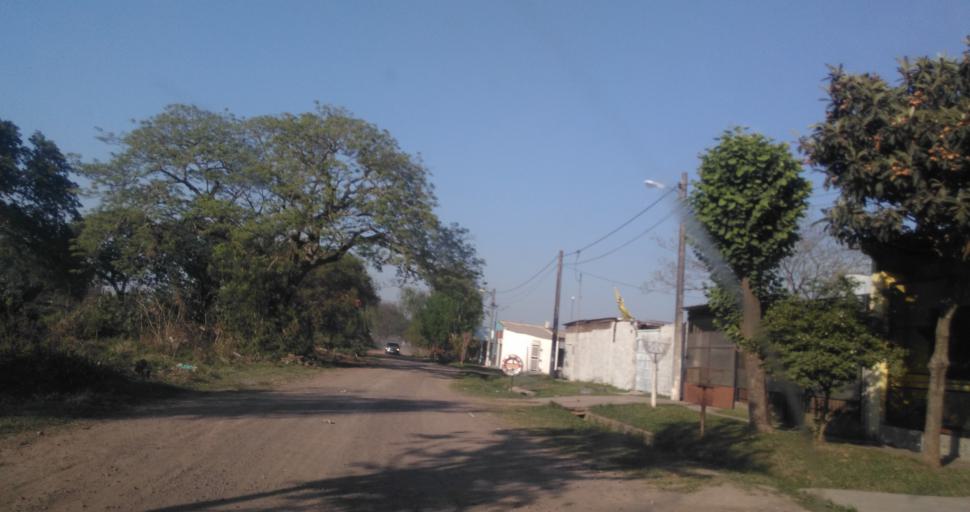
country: AR
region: Chaco
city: Fontana
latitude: -27.4116
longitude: -59.0317
